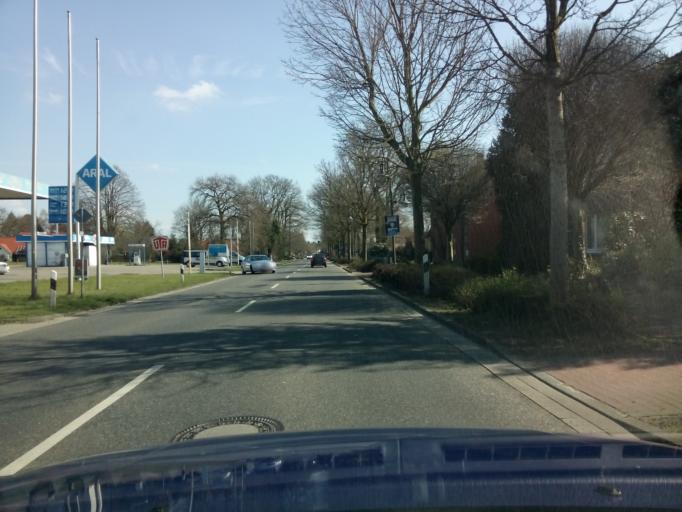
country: DE
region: Lower Saxony
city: Emlichheim
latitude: 52.6073
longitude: 6.8386
